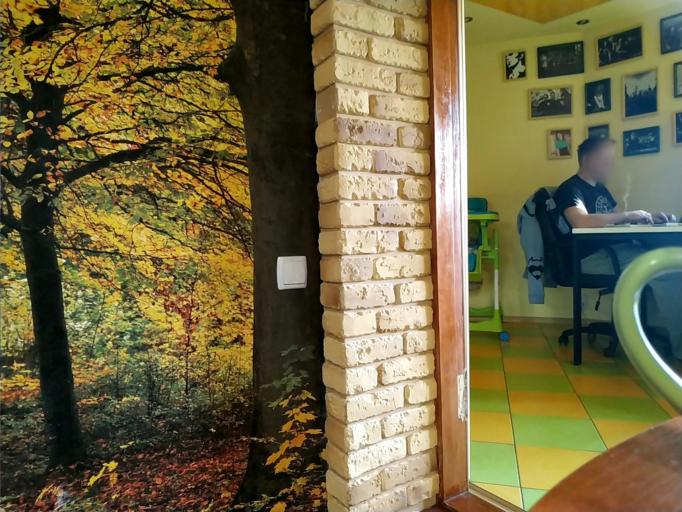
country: RU
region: Jaroslavl
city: Krasnyy Profintern
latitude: 57.8502
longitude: 40.6215
